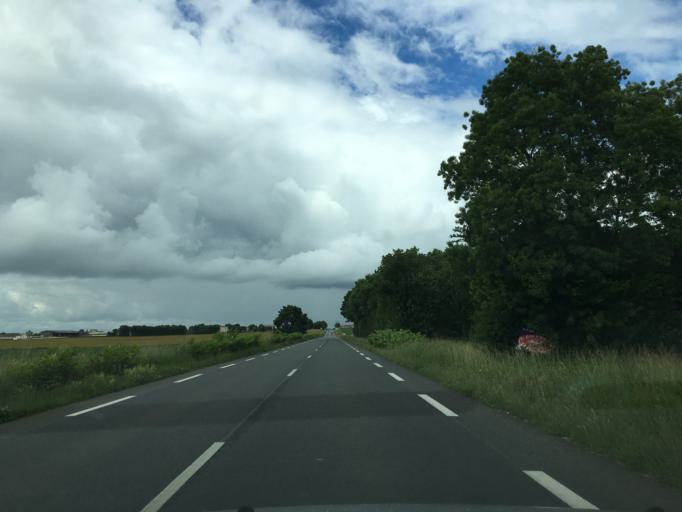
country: FR
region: Poitou-Charentes
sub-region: Departement de la Charente-Maritime
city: Saint-Jean-d'Angely
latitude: 46.0660
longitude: -0.5079
